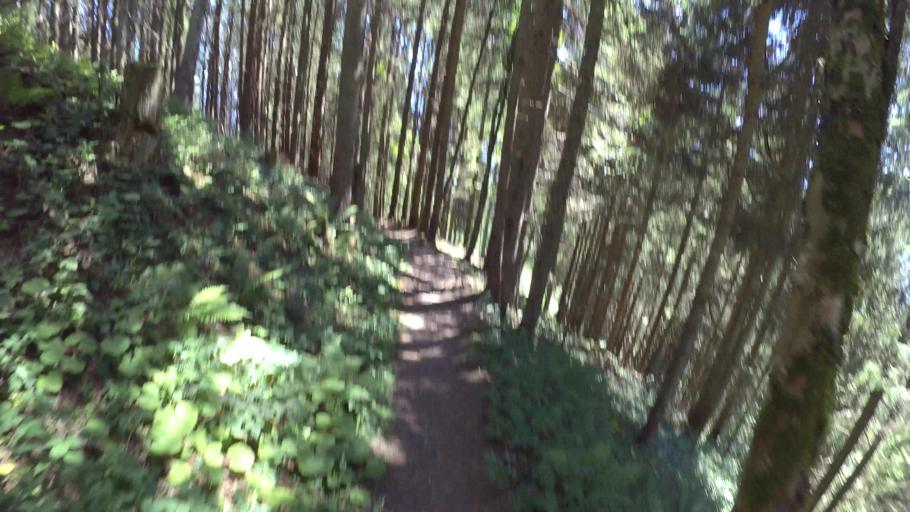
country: AT
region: Salzburg
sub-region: Politischer Bezirk Sankt Johann im Pongau
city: Goldegg
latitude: 47.3347
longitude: 13.0663
